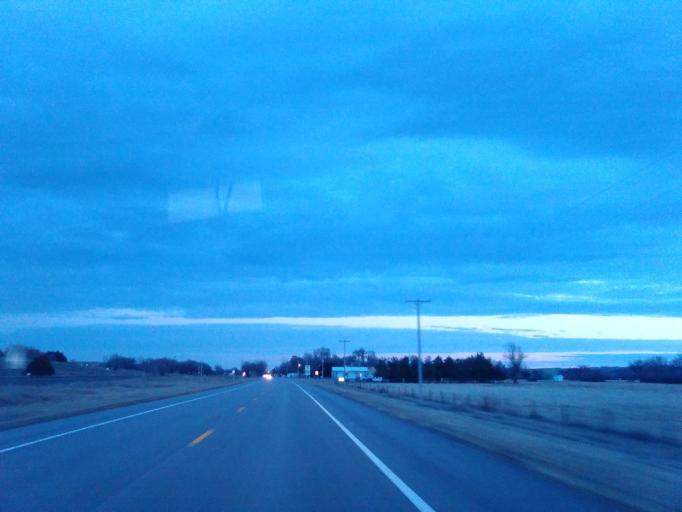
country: US
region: Nebraska
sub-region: Garden County
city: Oshkosh
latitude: 41.3367
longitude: -102.1555
